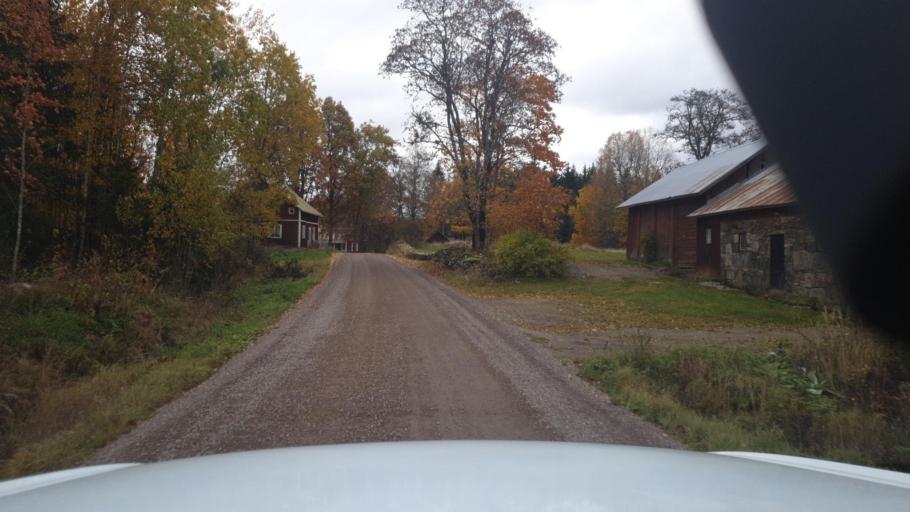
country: SE
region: Vaermland
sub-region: Arvika Kommun
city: Arvika
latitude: 59.9732
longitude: 12.6590
